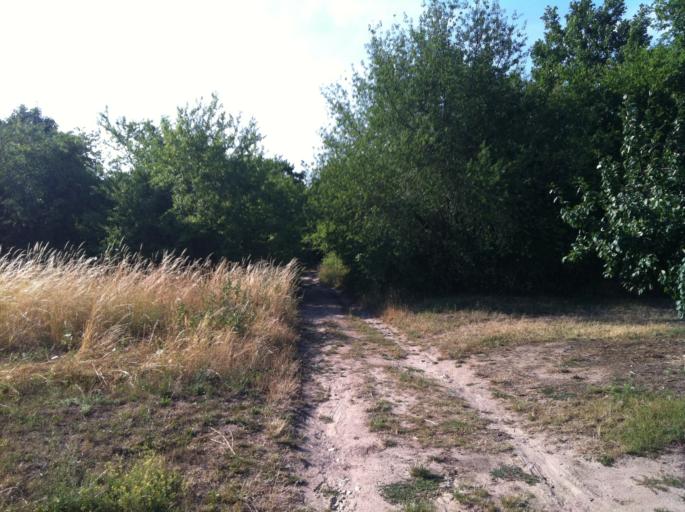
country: DE
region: Rheinland-Pfalz
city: Budenheim
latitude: 49.9984
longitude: 8.1562
